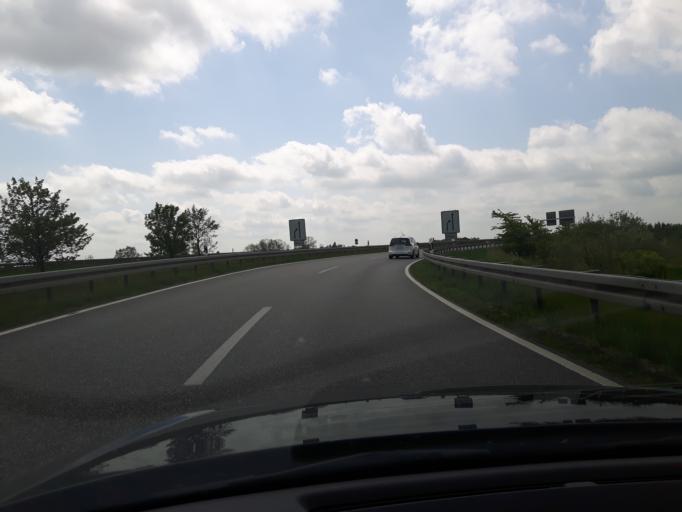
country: DE
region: Mecklenburg-Vorpommern
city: Kavelstorf
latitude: 54.0288
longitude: 12.1976
